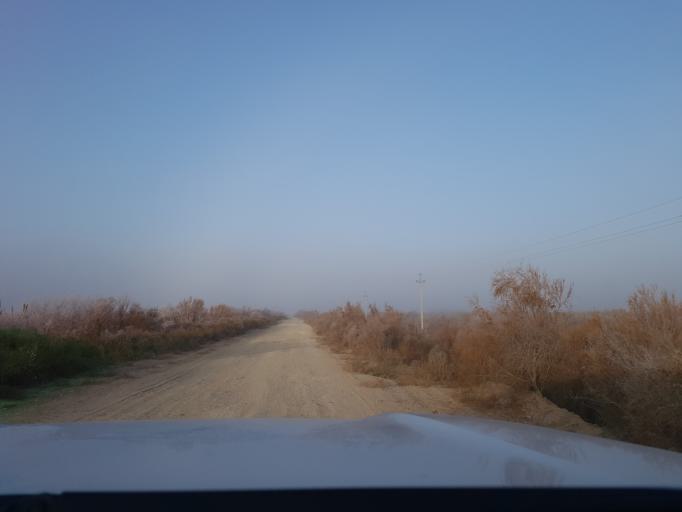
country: TM
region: Dasoguz
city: Koeneuergench
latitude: 41.8481
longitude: 58.3498
